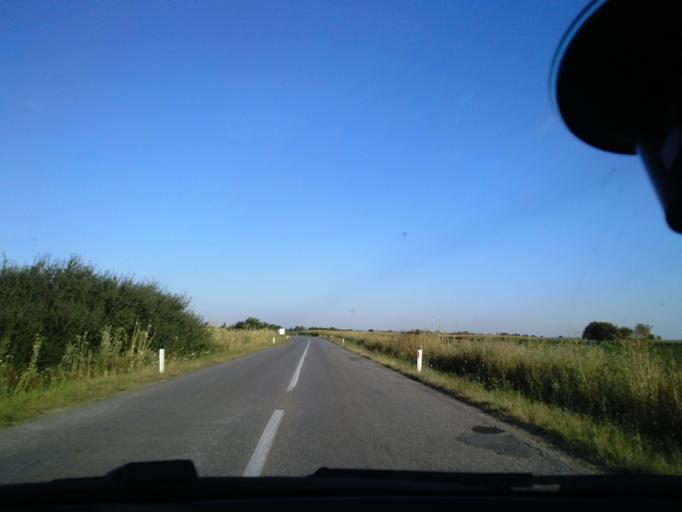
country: RS
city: Obrovac
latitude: 45.4264
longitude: 19.3873
